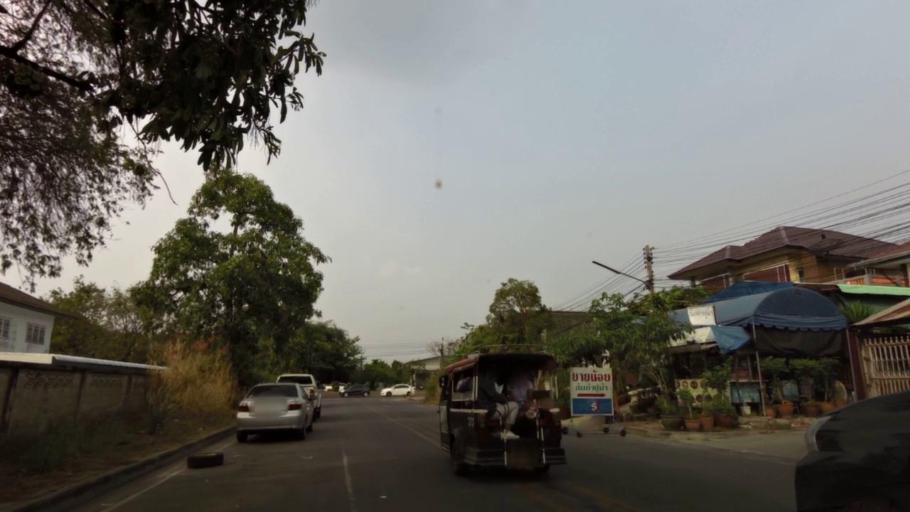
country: TH
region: Phra Nakhon Si Ayutthaya
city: Phra Nakhon Si Ayutthaya
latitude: 14.3501
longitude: 100.5714
